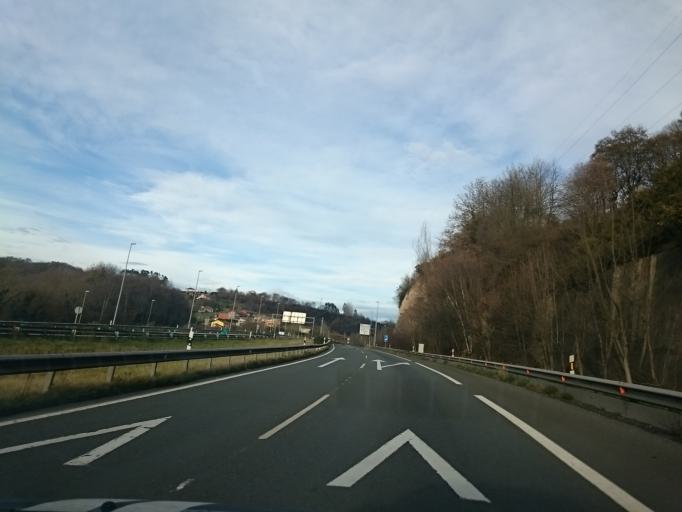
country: ES
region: Asturias
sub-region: Province of Asturias
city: Oviedo
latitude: 43.3233
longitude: -5.8733
